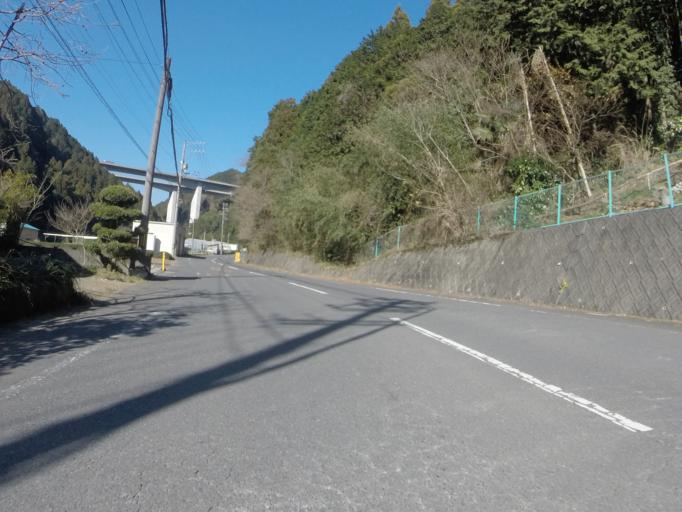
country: JP
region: Shizuoka
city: Fujinomiya
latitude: 35.1103
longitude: 138.4899
